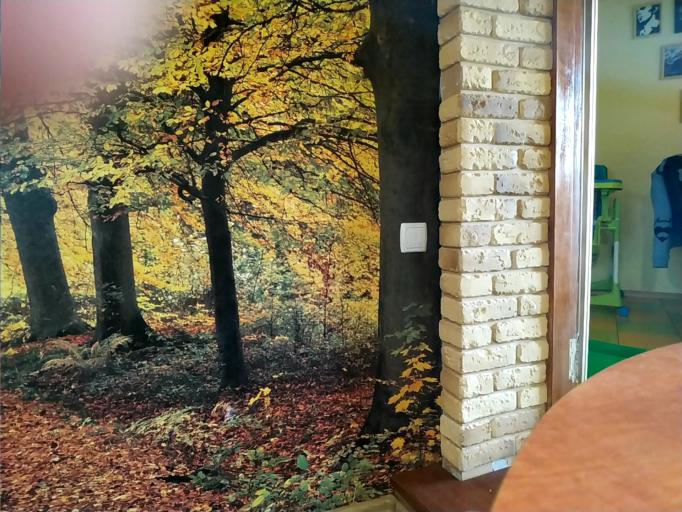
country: RU
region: Leningrad
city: Luga
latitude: 58.9677
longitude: 29.5577
